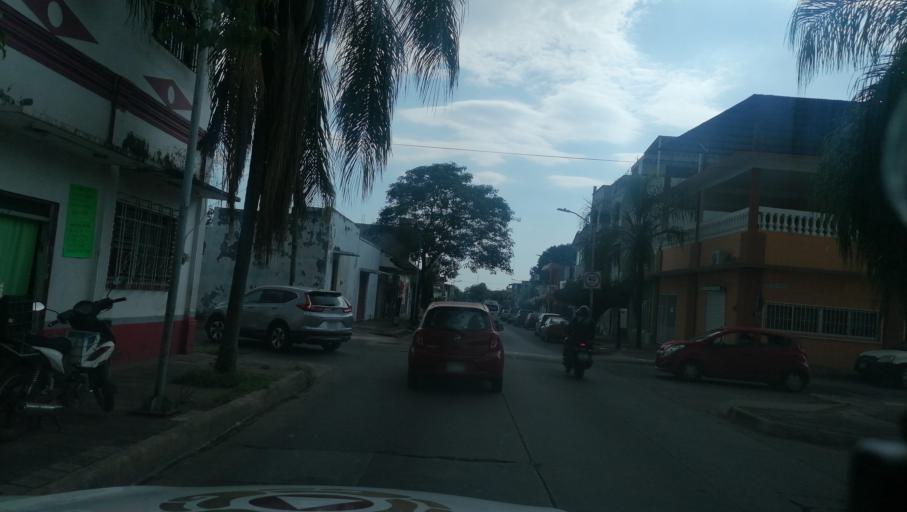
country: MX
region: Chiapas
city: Tapachula
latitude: 14.9082
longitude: -92.2574
